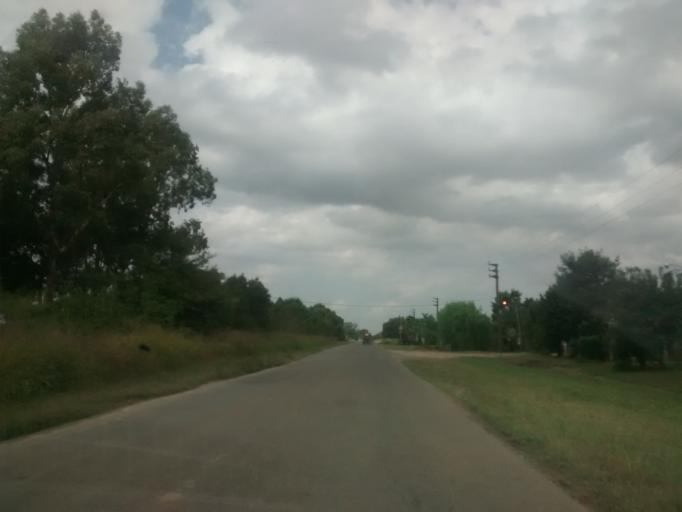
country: AR
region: Buenos Aires
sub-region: Partido de La Plata
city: La Plata
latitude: -34.9888
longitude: -57.9196
